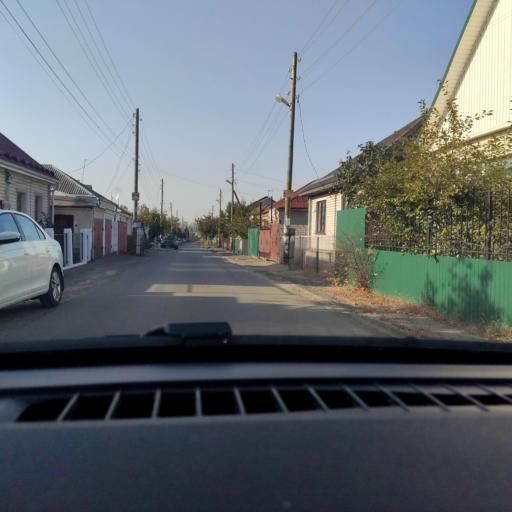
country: RU
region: Voronezj
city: Voronezh
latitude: 51.6282
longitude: 39.1709
